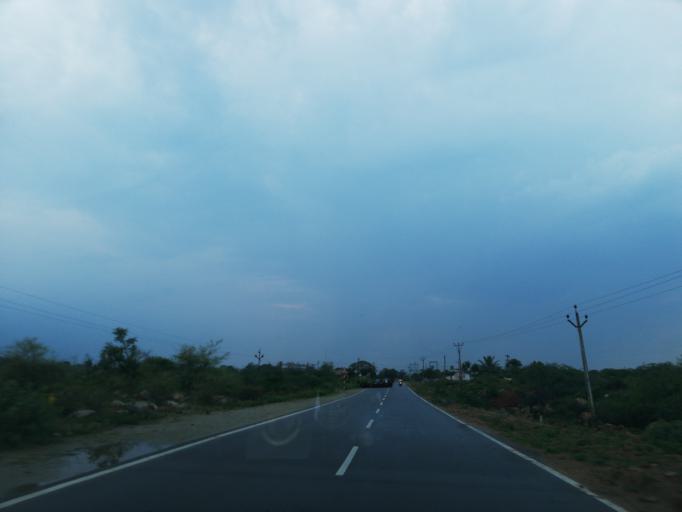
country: IN
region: Andhra Pradesh
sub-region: Guntur
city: Macherla
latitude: 16.6700
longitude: 79.2800
